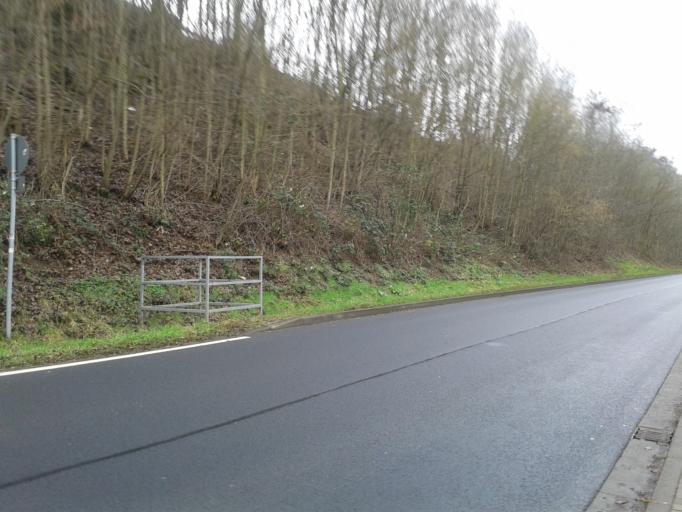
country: DE
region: Hesse
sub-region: Regierungsbezirk Darmstadt
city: Schluchtern
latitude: 50.3436
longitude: 9.5134
